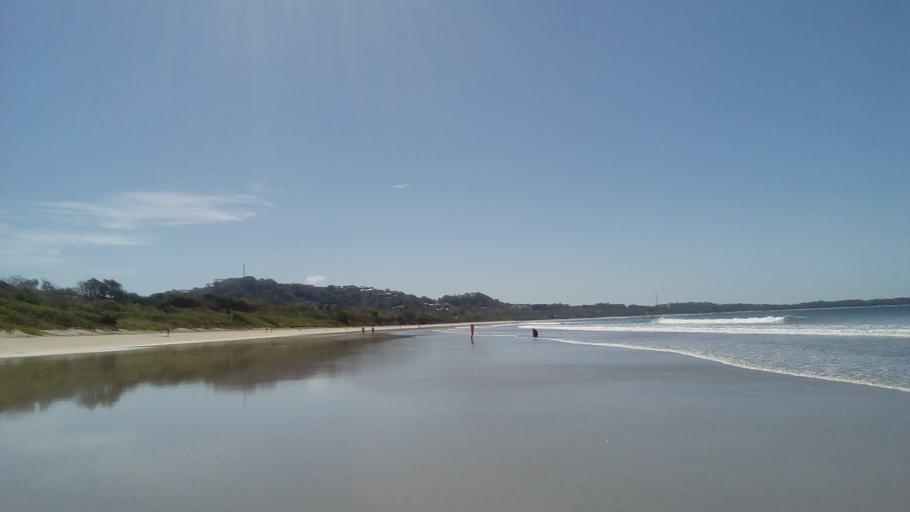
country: CR
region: Guanacaste
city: Santa Cruz
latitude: 10.3211
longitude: -85.8412
